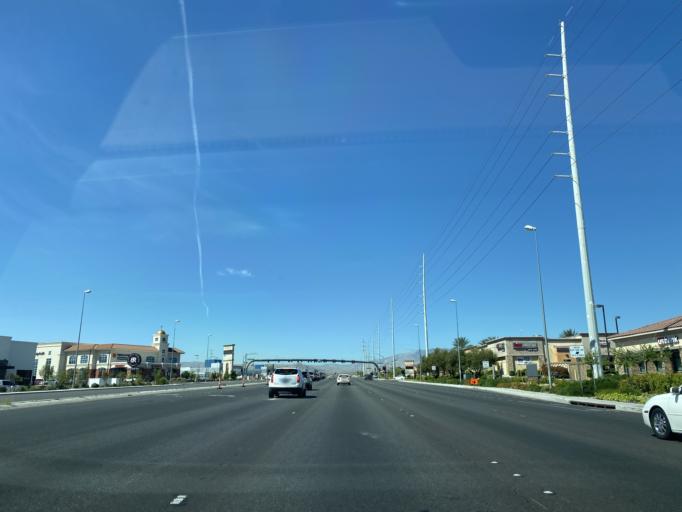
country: US
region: Nevada
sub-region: Clark County
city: Enterprise
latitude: 36.0339
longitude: -115.2051
